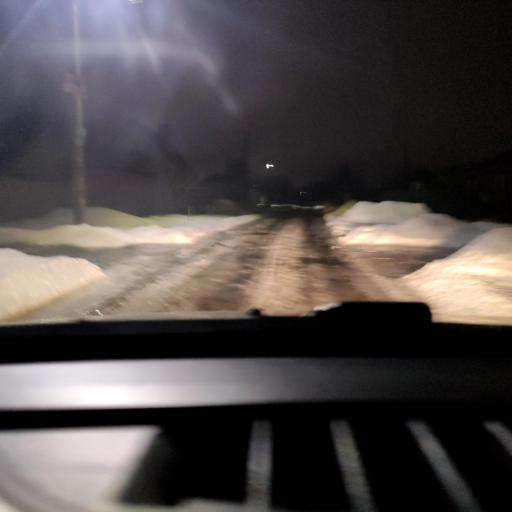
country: RU
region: Voronezj
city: Semiluki
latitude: 51.7343
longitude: 39.0447
